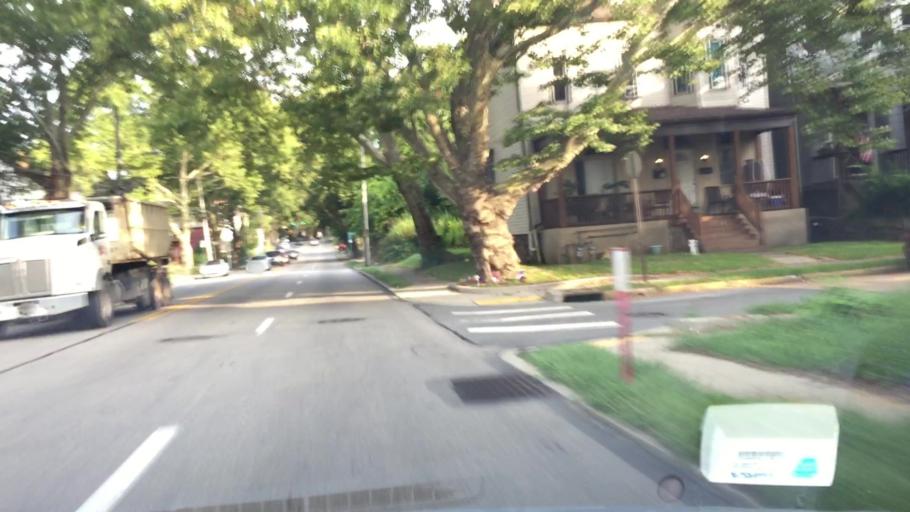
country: US
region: Pennsylvania
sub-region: Allegheny County
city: Avalon
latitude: 40.5000
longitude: -80.0727
